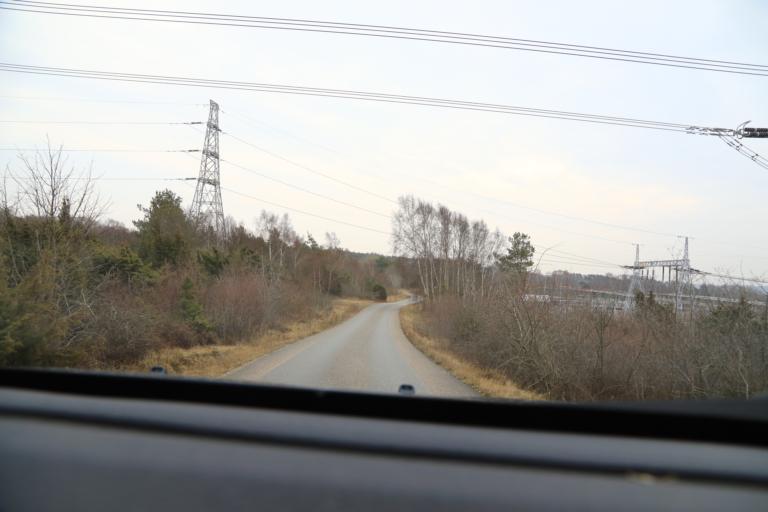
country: SE
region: Halland
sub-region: Kungsbacka Kommun
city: Frillesas
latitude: 57.2634
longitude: 12.1191
